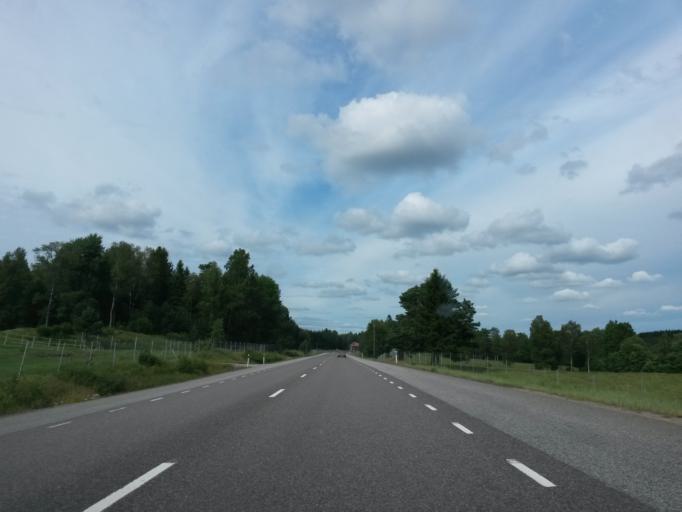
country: SE
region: Vaestra Goetaland
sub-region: Boras Kommun
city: Viskafors
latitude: 57.5796
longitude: 12.8587
